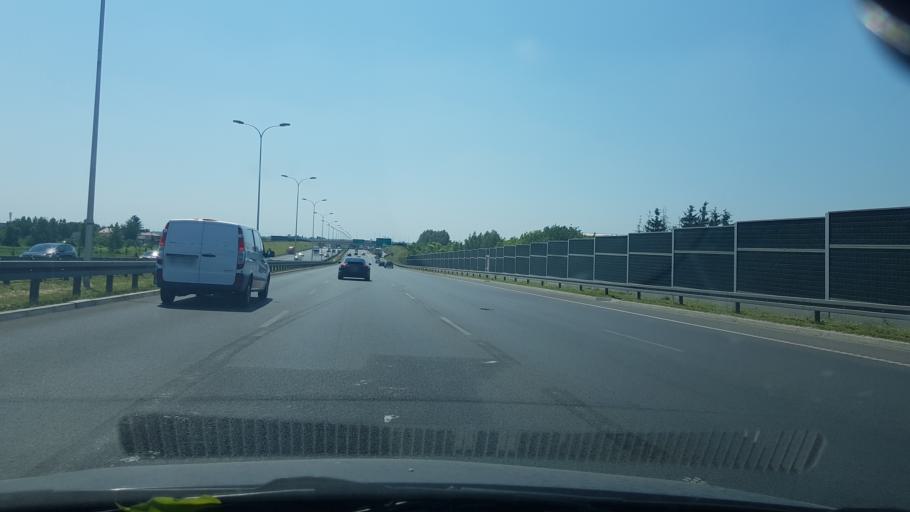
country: PL
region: Masovian Voivodeship
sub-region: Powiat pruszkowski
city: Nowe Grocholice
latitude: 52.1829
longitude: 20.9157
